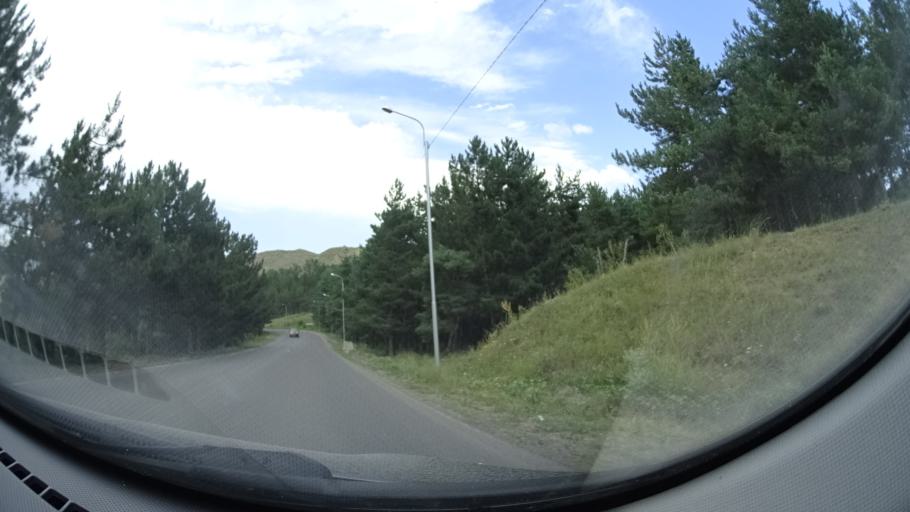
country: GE
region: Samtskhe-Javakheti
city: Aspindza
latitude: 41.5805
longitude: 43.2439
